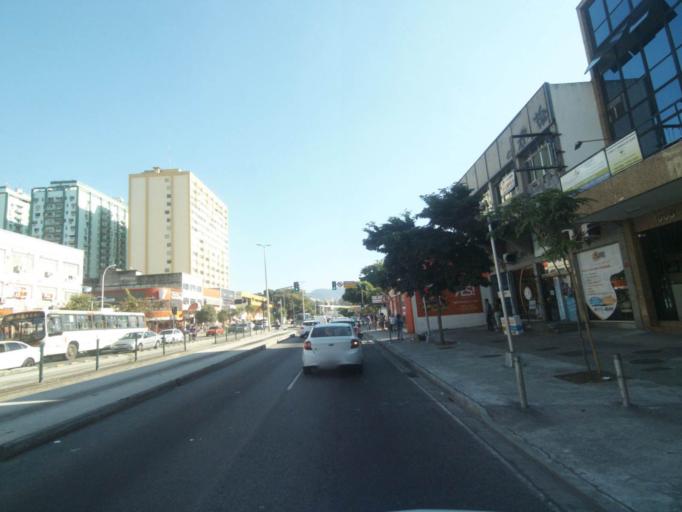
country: BR
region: Rio de Janeiro
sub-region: Sao Joao De Meriti
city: Sao Joao de Meriti
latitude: -22.9210
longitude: -43.3700
